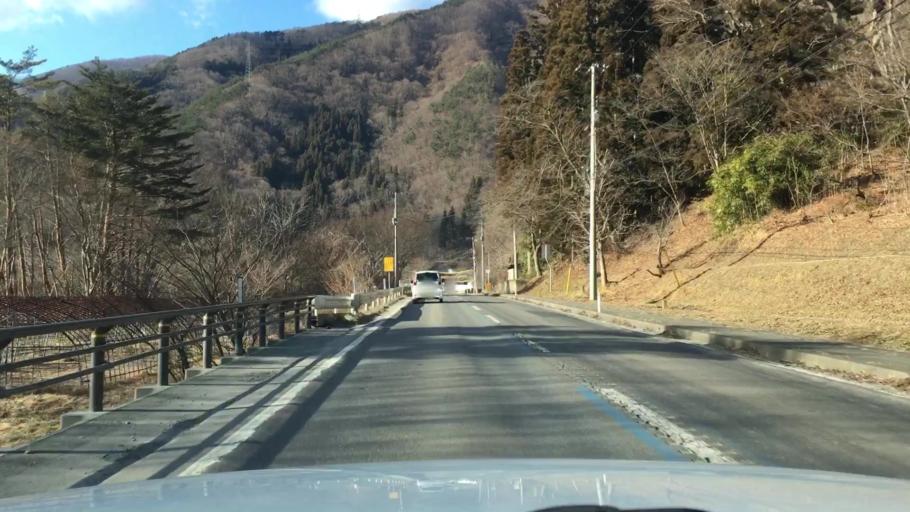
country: JP
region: Iwate
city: Miyako
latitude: 39.6024
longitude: 141.7011
